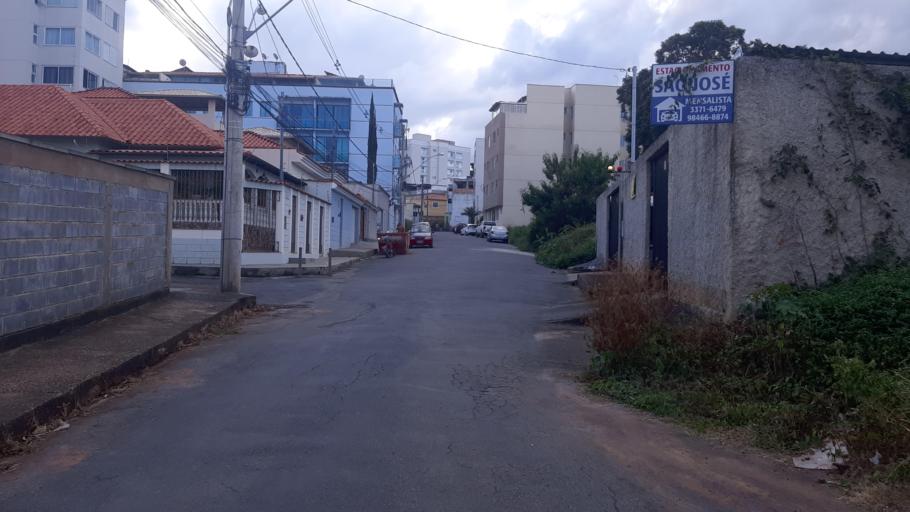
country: BR
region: Minas Gerais
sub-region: Sao Joao Del Rei
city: Sao Joao del Rei
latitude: -21.1263
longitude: -44.2517
